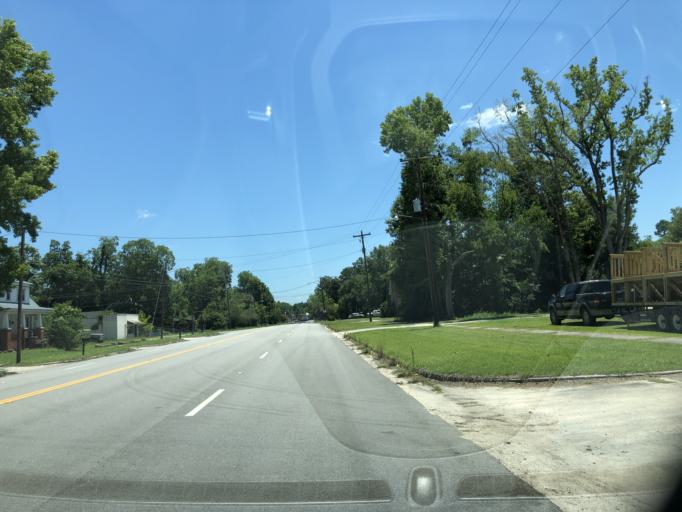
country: US
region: South Carolina
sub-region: Orangeburg County
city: Branchville
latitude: 33.2507
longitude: -80.8221
